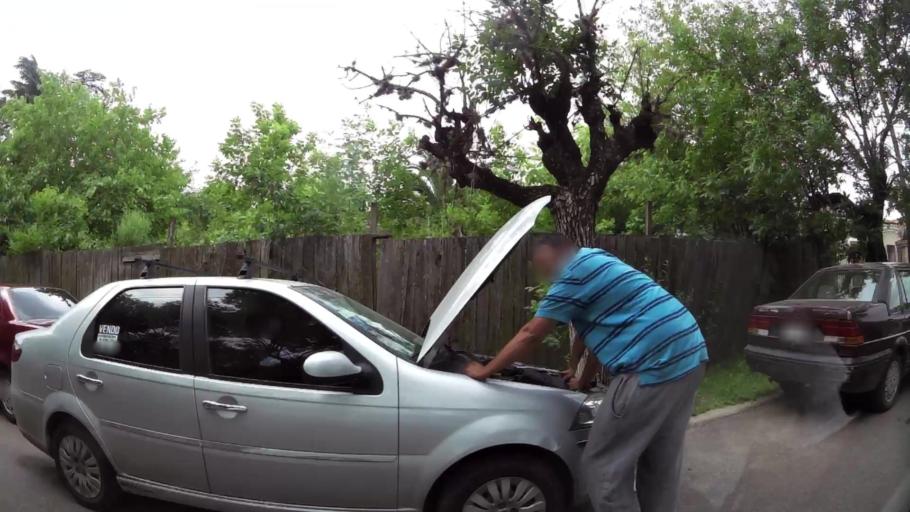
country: AR
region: Buenos Aires
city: San Justo
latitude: -34.7369
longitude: -58.5262
